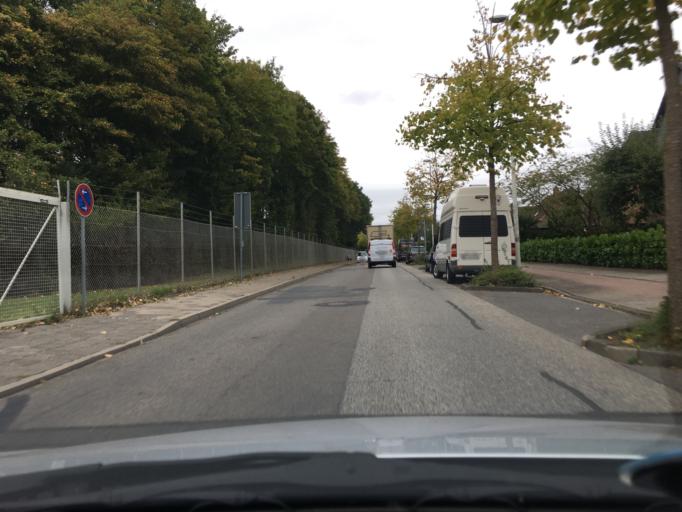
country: DE
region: Schleswig-Holstein
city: Kronshagen
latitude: 54.3377
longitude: 10.0934
